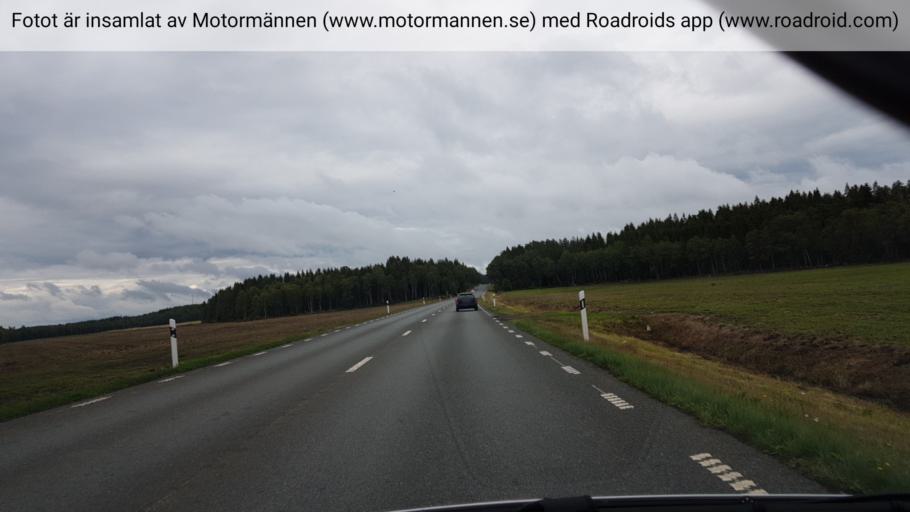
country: SE
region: Vaestra Goetaland
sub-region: Tidaholms Kommun
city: Tidaholm
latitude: 58.1341
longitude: 13.8776
